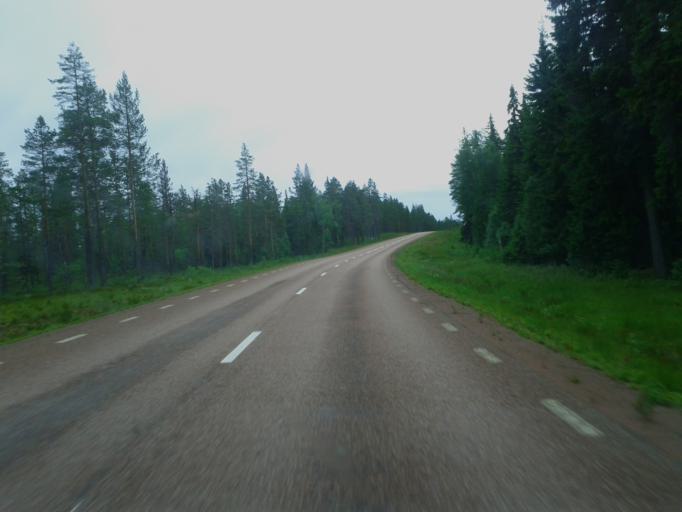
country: SE
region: Dalarna
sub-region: Alvdalens Kommun
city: AElvdalen
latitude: 61.4838
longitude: 13.4231
